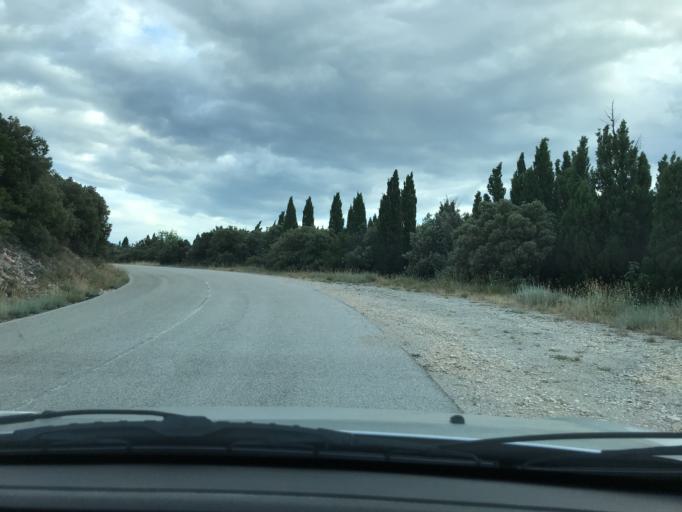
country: IT
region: Umbria
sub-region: Provincia di Terni
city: Montecchio
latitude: 42.6907
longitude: 12.2954
